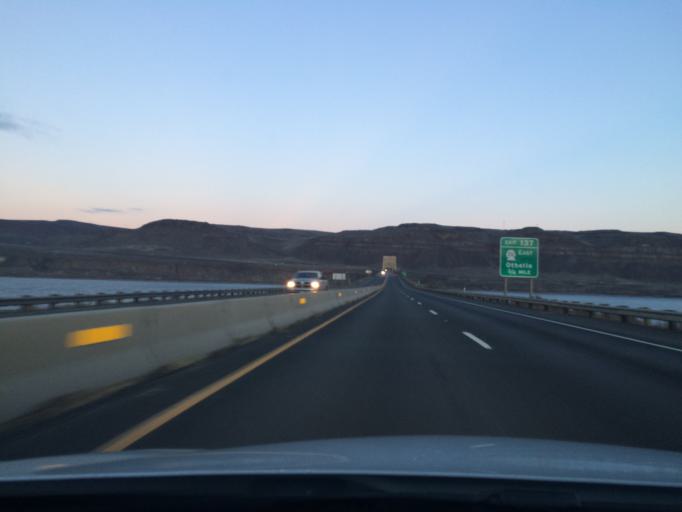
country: US
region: Washington
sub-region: Grant County
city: Mattawa
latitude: 46.9407
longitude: -119.9791
